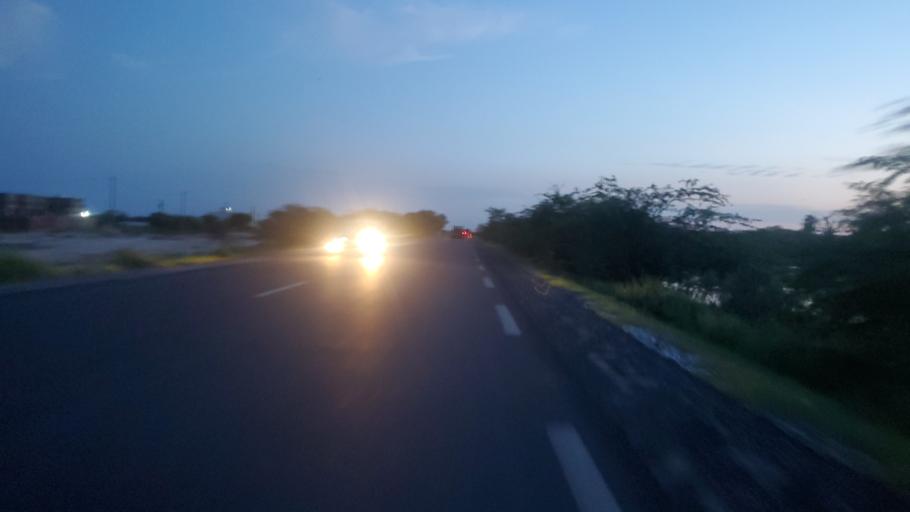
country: SN
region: Saint-Louis
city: Saint-Louis
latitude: 16.0611
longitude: -16.3959
